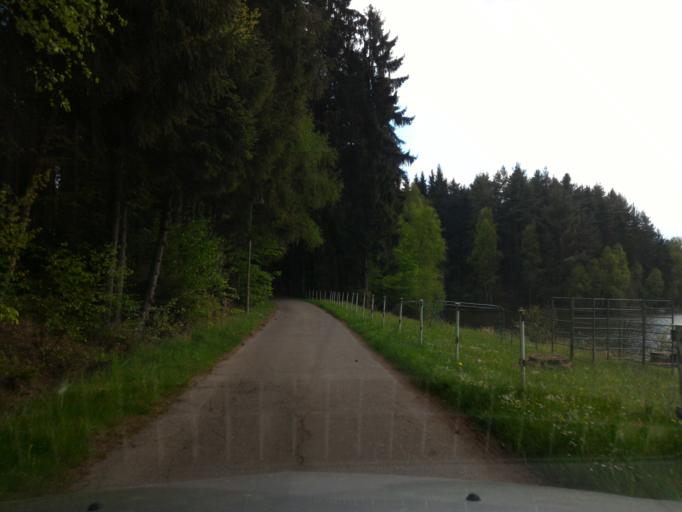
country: CZ
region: Vysocina
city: Ledec nad Sazavou
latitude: 49.6347
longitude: 15.3023
